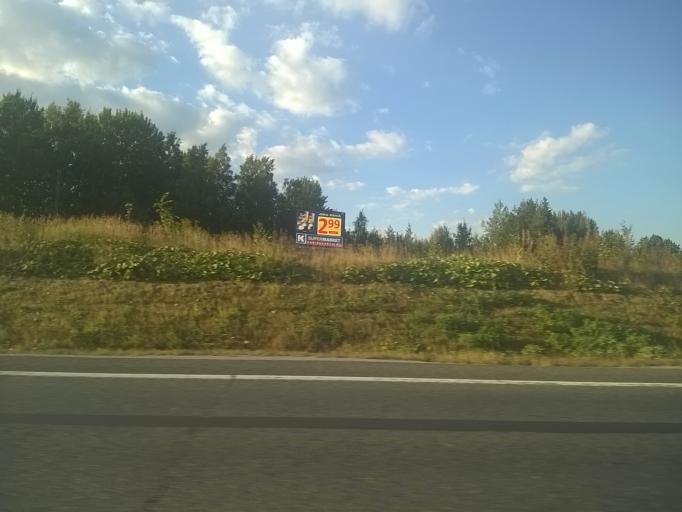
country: FI
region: Pirkanmaa
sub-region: Tampere
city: Tampere
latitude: 61.4629
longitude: 23.7651
